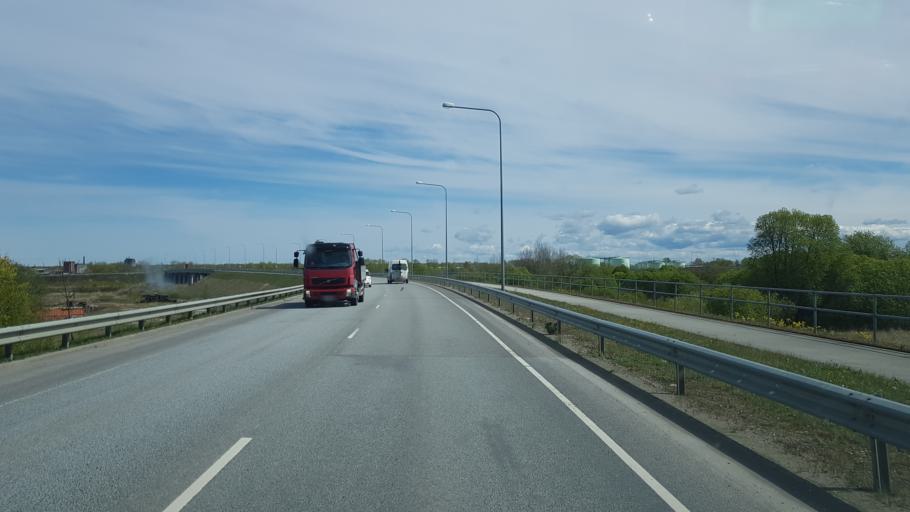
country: EE
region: Harju
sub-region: Joelaehtme vald
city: Loo
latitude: 59.4532
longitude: 24.9728
